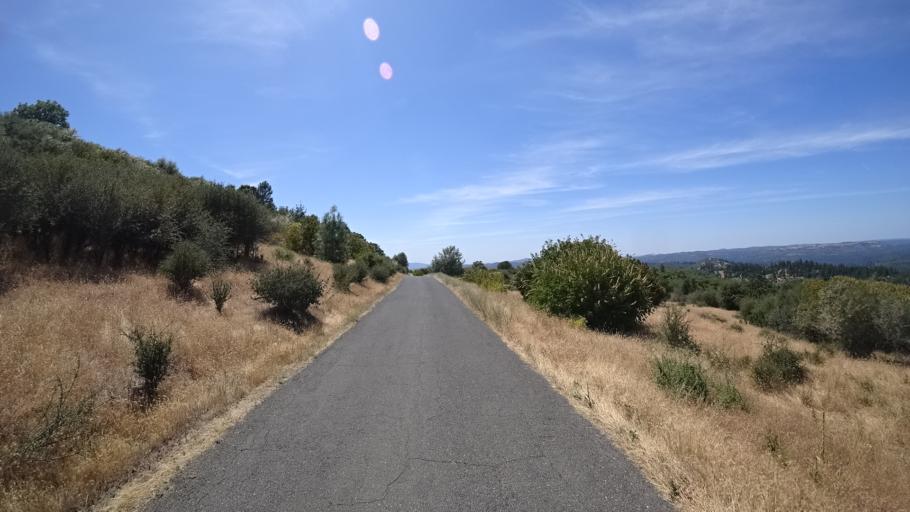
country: US
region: California
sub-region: Calaveras County
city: Forest Meadows
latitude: 38.1804
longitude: -120.4347
